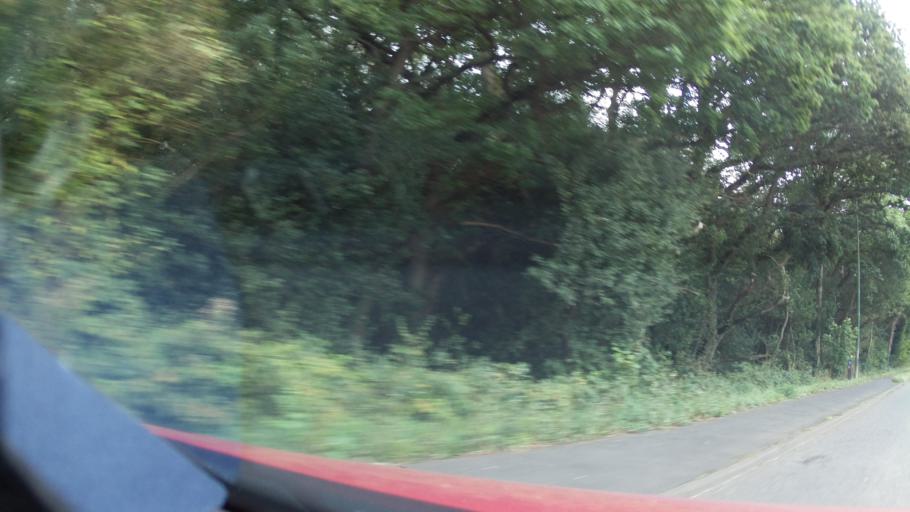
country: GB
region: England
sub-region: Solihull
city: Cheswick Green
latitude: 52.3755
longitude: -1.7852
